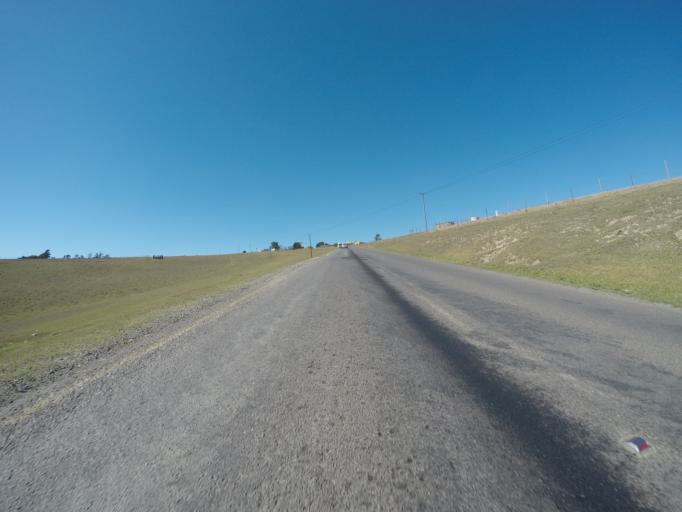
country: ZA
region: Eastern Cape
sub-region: OR Tambo District Municipality
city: Mthatha
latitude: -31.7801
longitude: 28.7380
